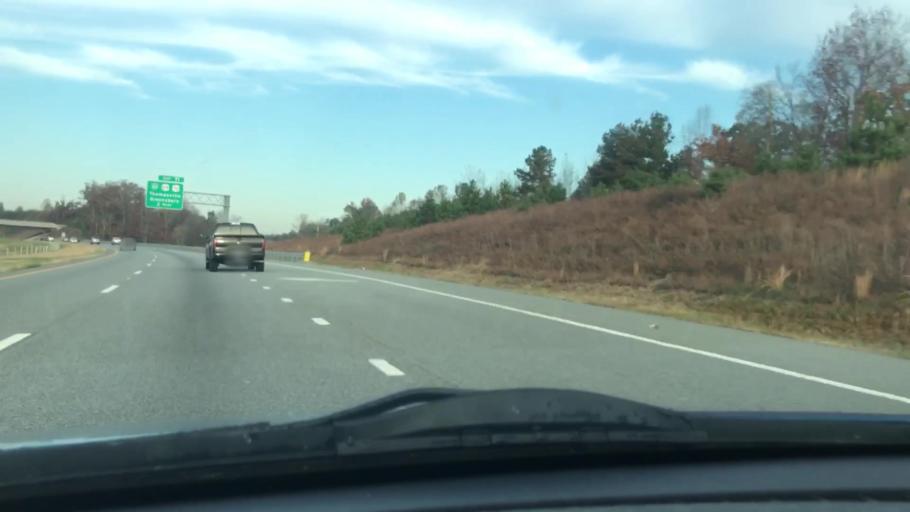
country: US
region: North Carolina
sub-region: Randolph County
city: Archdale
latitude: 35.9355
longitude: -79.9325
